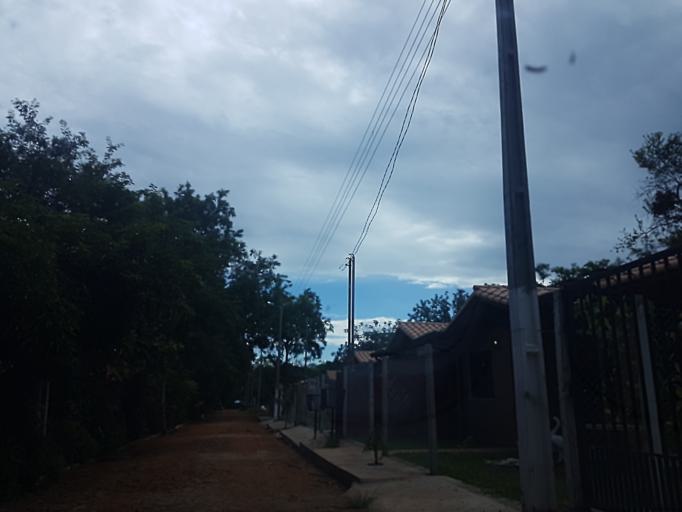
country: PY
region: Central
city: Limpio
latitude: -25.2400
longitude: -57.4461
